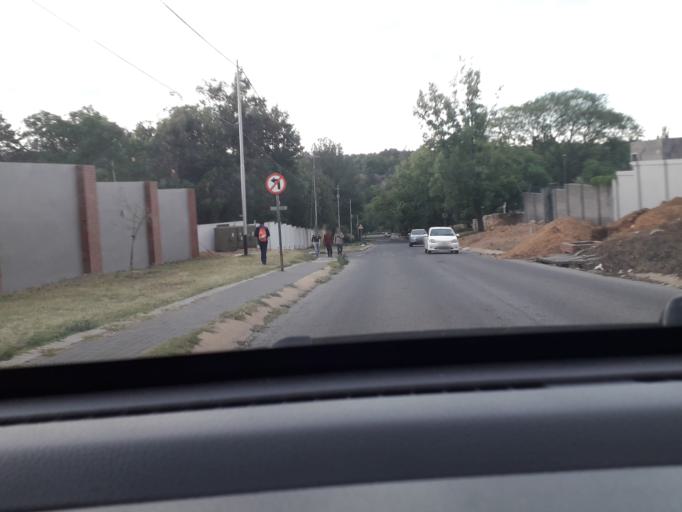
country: ZA
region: Gauteng
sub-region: City of Johannesburg Metropolitan Municipality
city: Midrand
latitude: -26.0578
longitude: 28.0529
